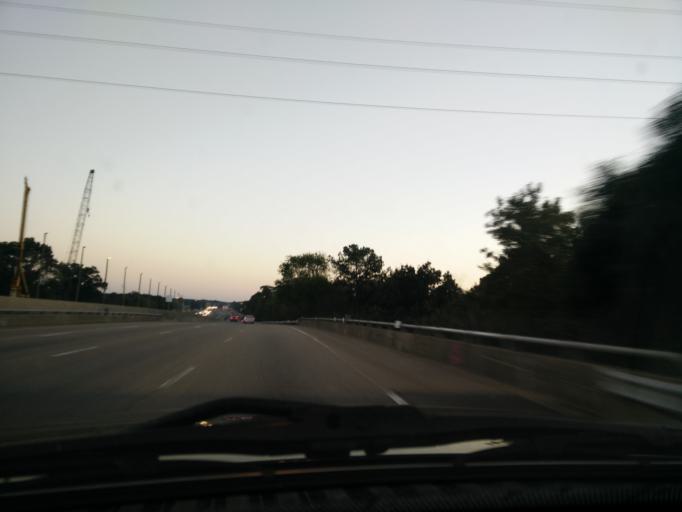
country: US
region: Virginia
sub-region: City of Chesapeake
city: Chesapeake
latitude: 36.8414
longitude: -76.1968
